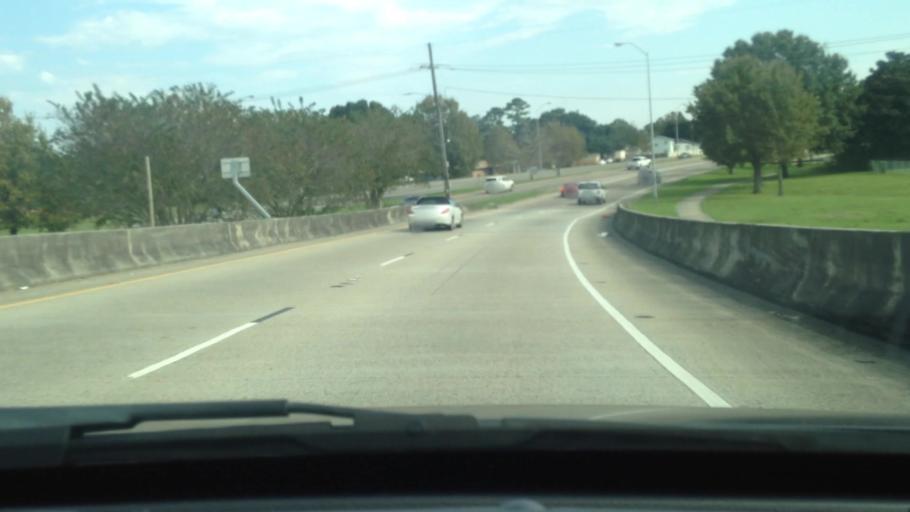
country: US
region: Louisiana
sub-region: Jefferson Parish
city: Terrytown
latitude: 29.9300
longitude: -90.0358
